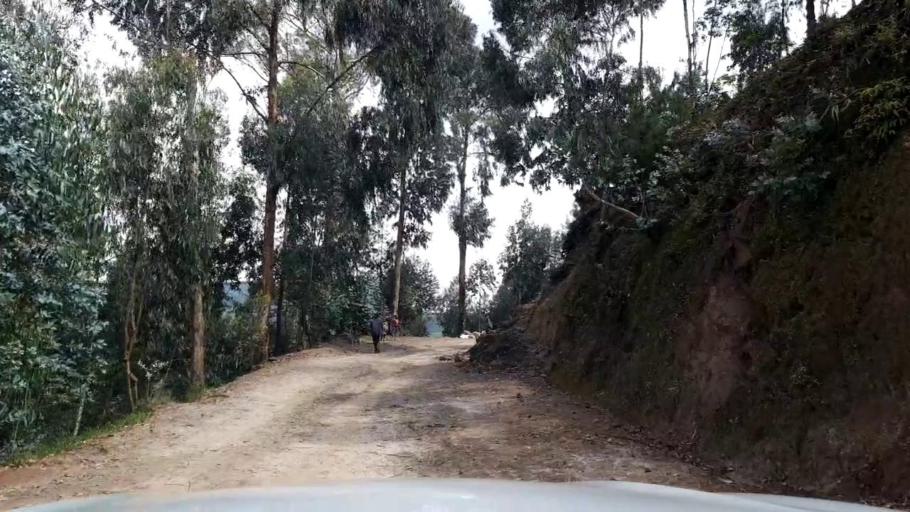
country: RW
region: Western Province
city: Kibuye
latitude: -1.9593
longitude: 29.4767
